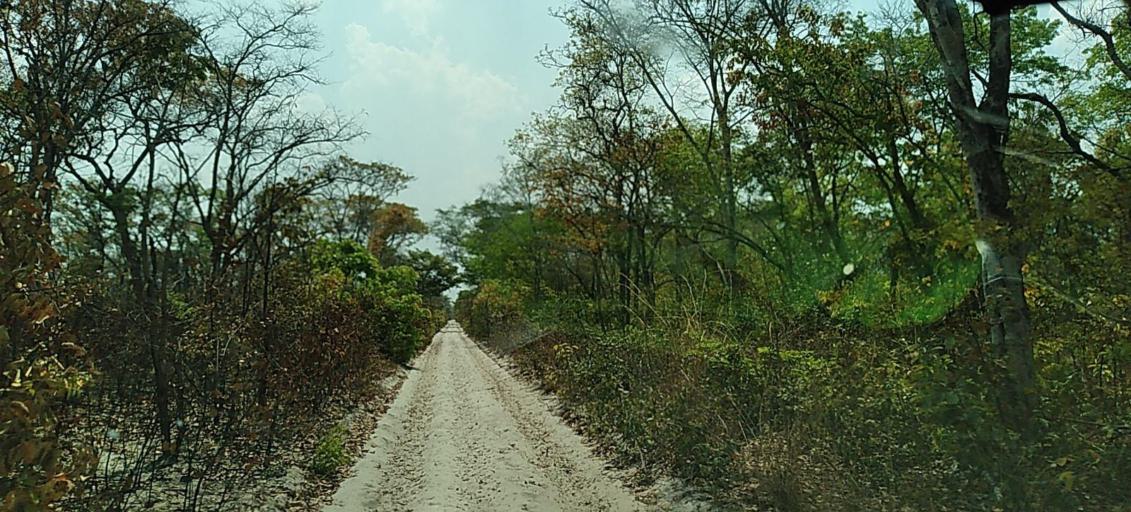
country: ZM
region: North-Western
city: Kabompo
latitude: -13.3931
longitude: 23.7905
